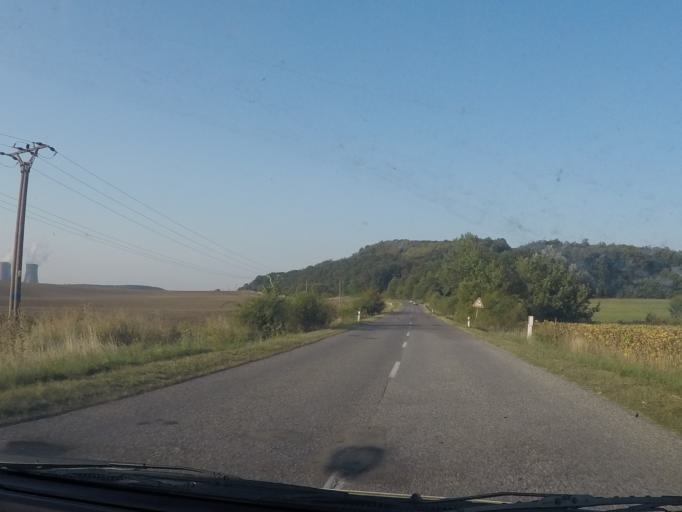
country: SK
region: Nitriansky
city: Tlmace
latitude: 48.2832
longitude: 18.4497
